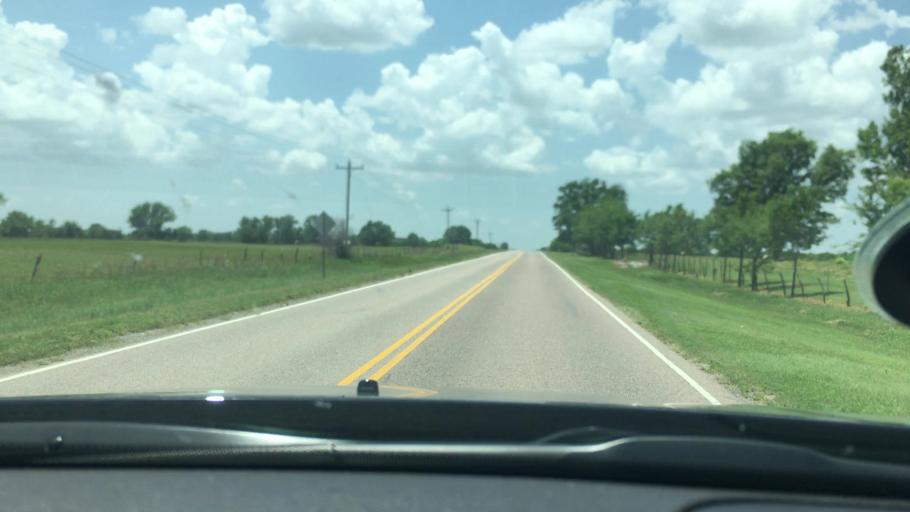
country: US
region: Oklahoma
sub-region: Johnston County
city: Tishomingo
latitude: 34.4808
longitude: -96.6288
